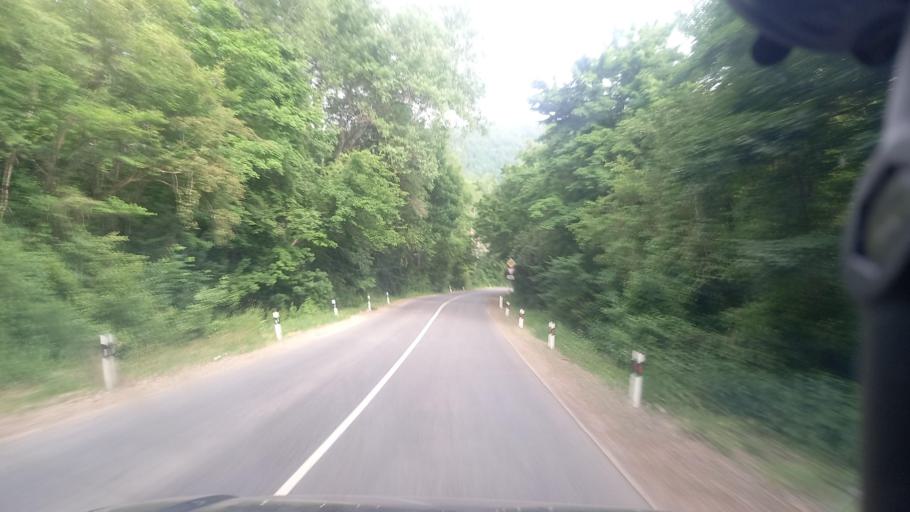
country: RU
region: Krasnodarskiy
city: Goryachiy Klyuch
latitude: 44.6000
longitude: 39.0465
